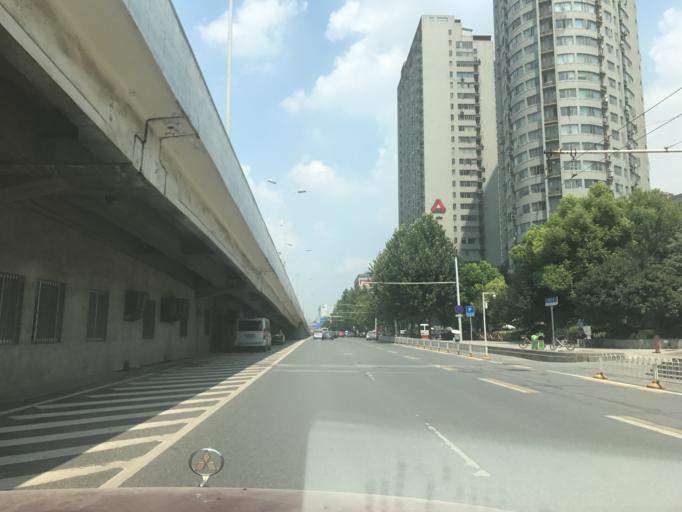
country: CN
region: Hubei
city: Jiang'an
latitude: 30.6169
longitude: 114.3024
